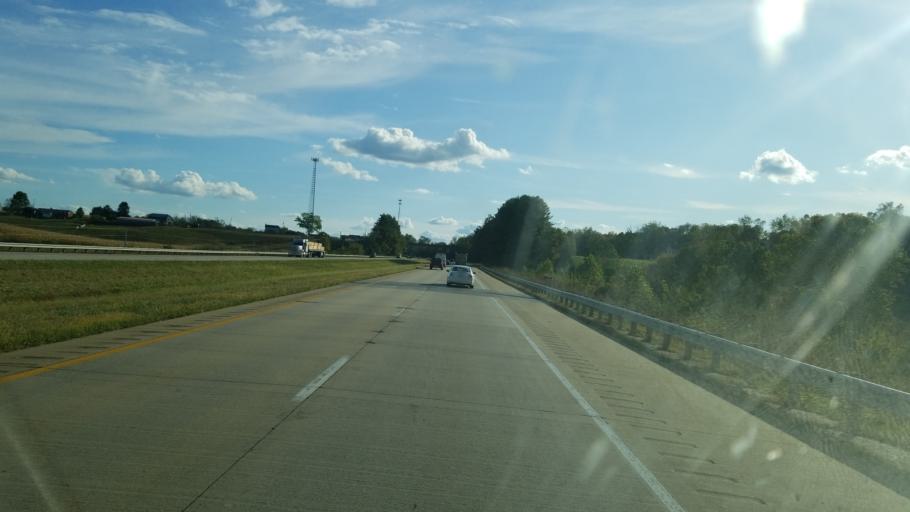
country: US
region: Ohio
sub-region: Washington County
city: Devola
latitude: 39.5169
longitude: -81.4515
